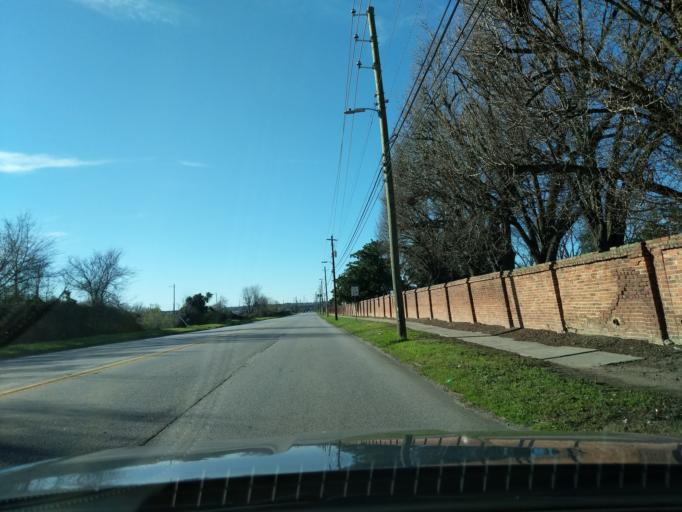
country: US
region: Georgia
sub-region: Richmond County
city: Augusta
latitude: 33.4581
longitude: -81.9579
